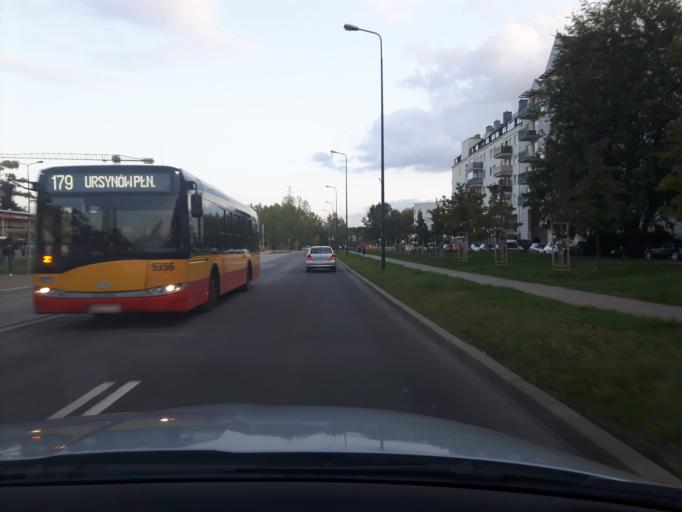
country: PL
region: Masovian Voivodeship
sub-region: Warszawa
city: Kabaty
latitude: 52.1293
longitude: 21.0676
